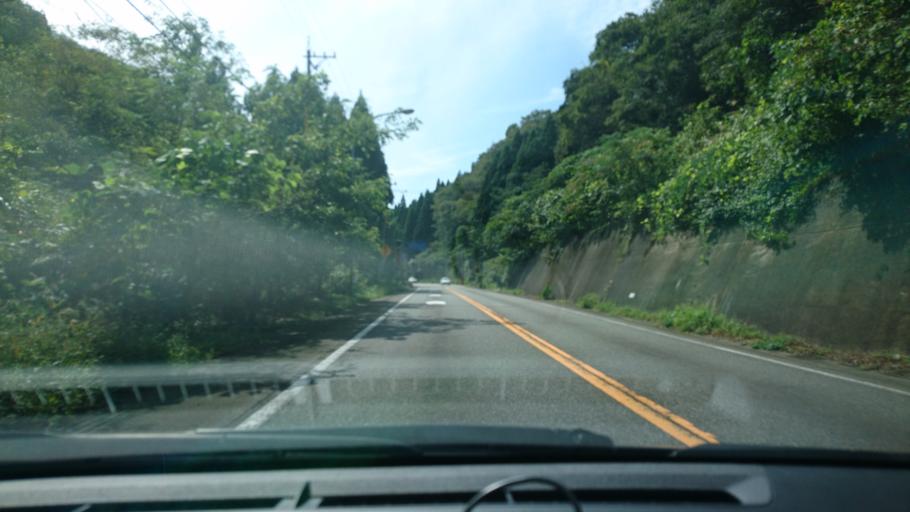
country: JP
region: Fukui
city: Maruoka
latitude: 36.2782
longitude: 136.2914
